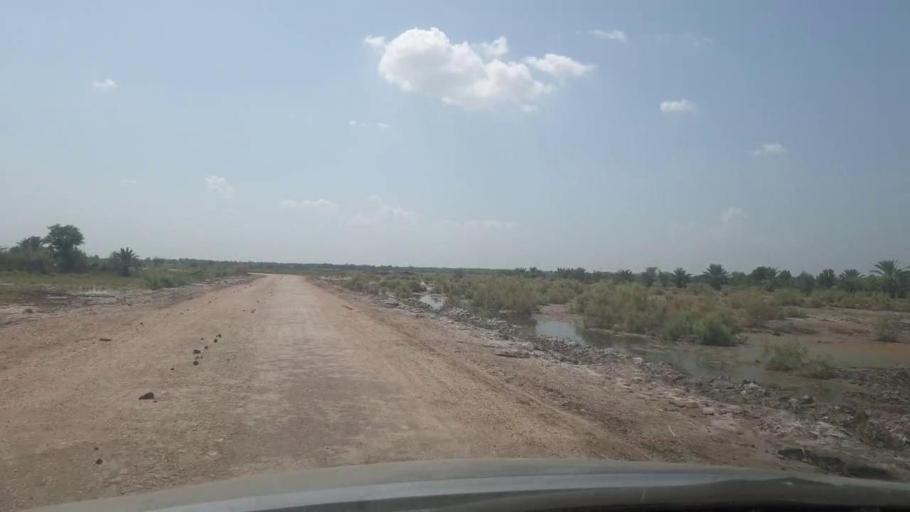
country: PK
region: Sindh
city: Khairpur
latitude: 27.5247
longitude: 68.8117
